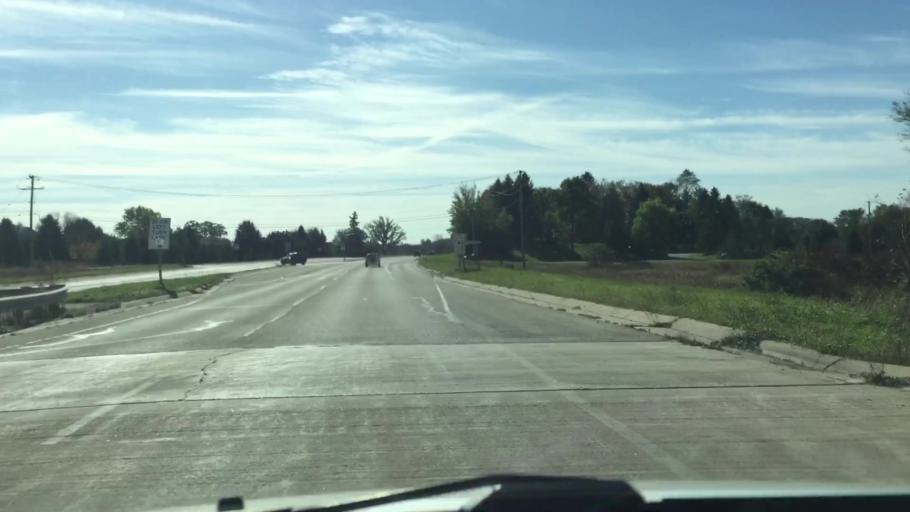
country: US
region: Wisconsin
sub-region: Waukesha County
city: Pewaukee
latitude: 43.1017
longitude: -88.2445
